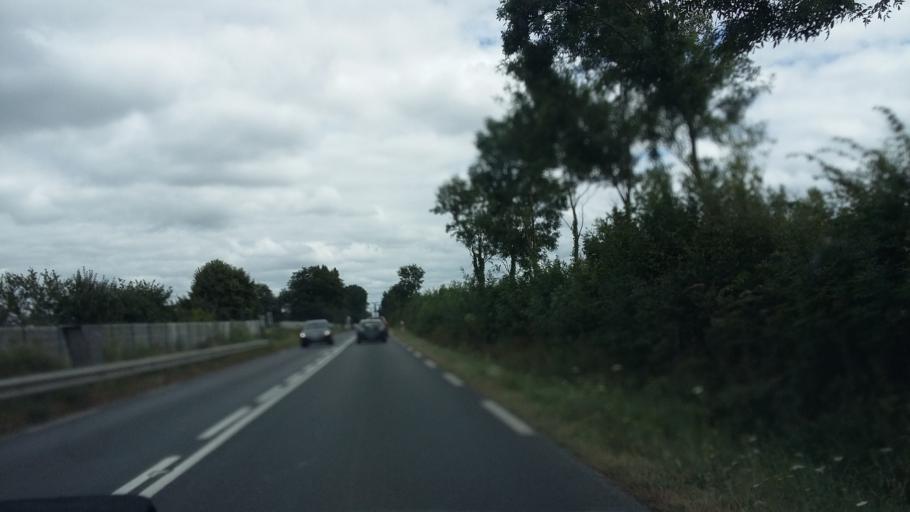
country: FR
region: Pays de la Loire
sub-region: Departement de la Vendee
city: Saint-Christophe-du-Ligneron
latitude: 46.8236
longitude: -1.7771
